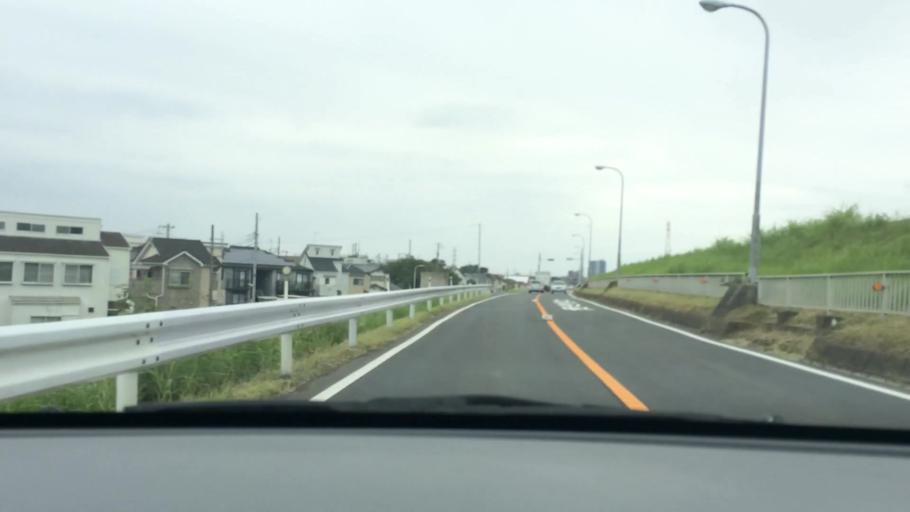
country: JP
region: Chiba
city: Matsudo
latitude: 35.7469
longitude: 139.8902
